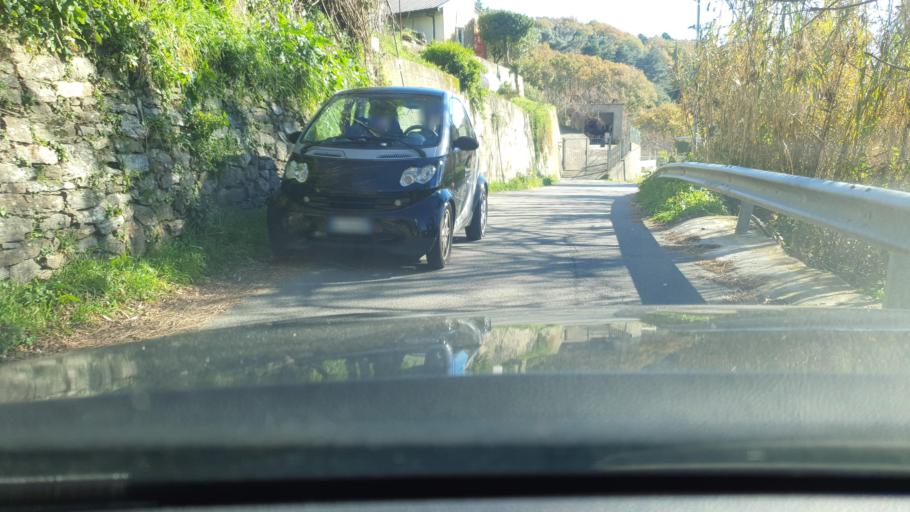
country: IT
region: Calabria
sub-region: Provincia di Catanzaro
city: Sant'Elia
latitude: 38.9569
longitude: 16.5805
